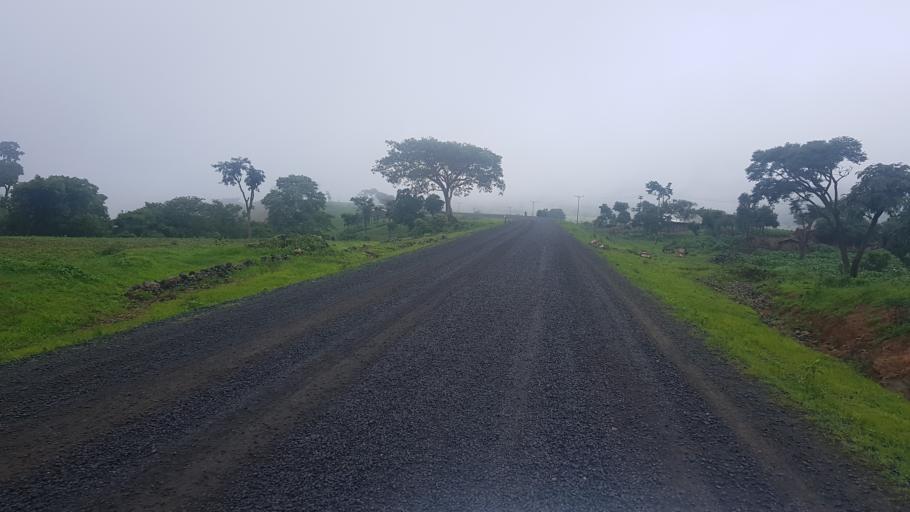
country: ET
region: Amhara
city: Bure
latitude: 10.1949
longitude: 36.9734
